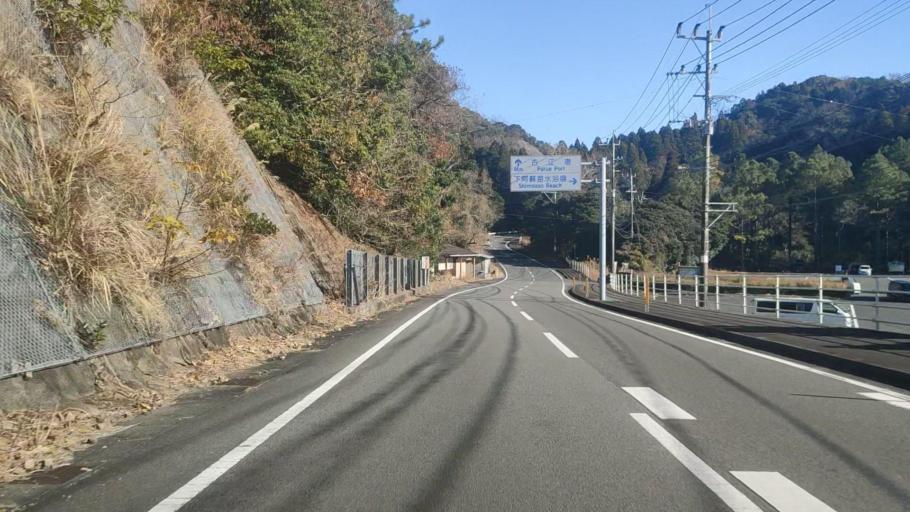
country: JP
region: Miyazaki
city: Nobeoka
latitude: 32.6853
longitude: 131.8029
